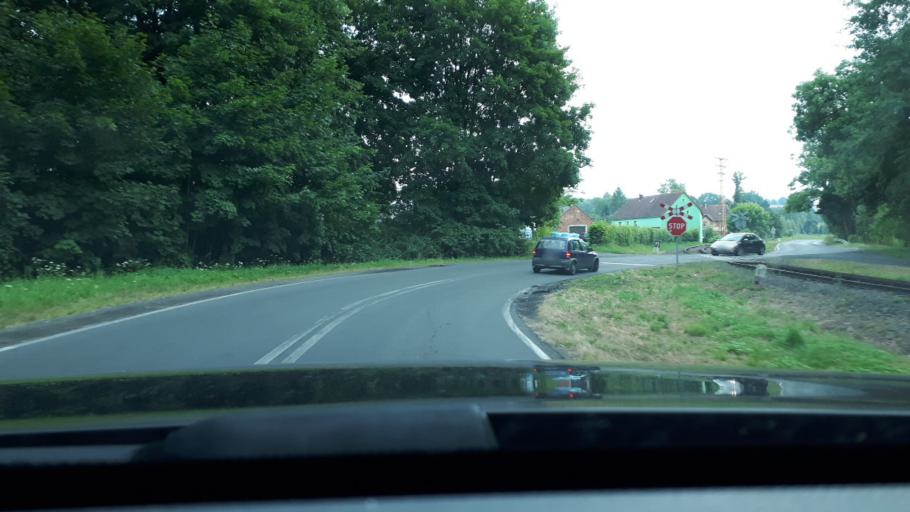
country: PL
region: Lower Silesian Voivodeship
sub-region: Powiat lubanski
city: Lesna
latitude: 51.0527
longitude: 15.2810
